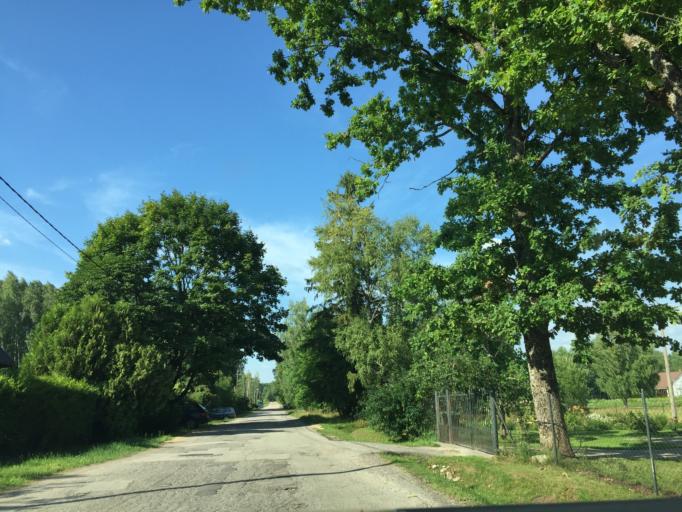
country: LV
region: Sigulda
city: Sigulda
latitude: 57.1609
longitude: 24.8654
